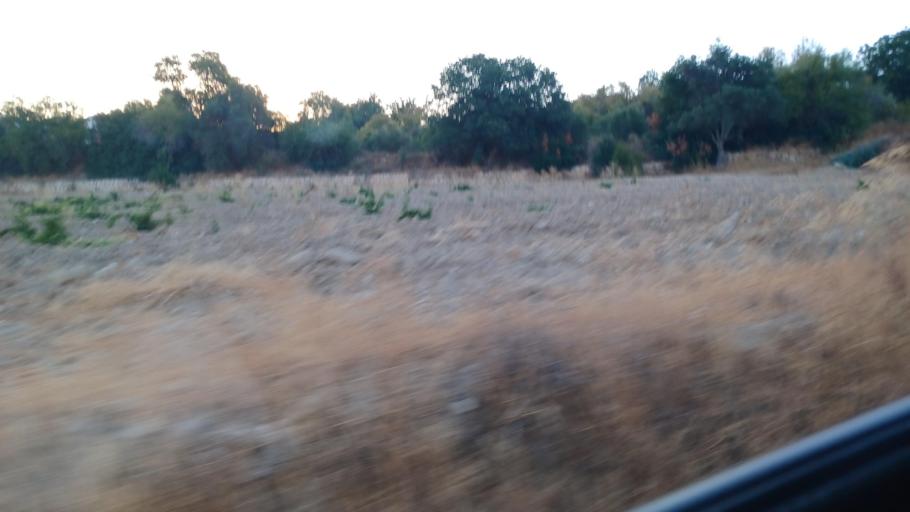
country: CY
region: Pafos
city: Mesogi
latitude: 34.8282
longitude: 32.5763
